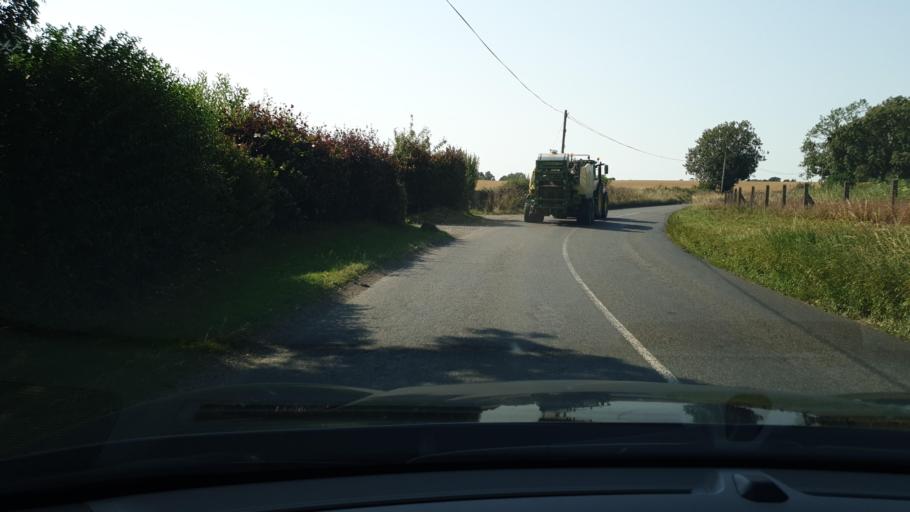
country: IE
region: Leinster
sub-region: An Mhi
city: Athboy
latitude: 53.5929
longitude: -6.8637
